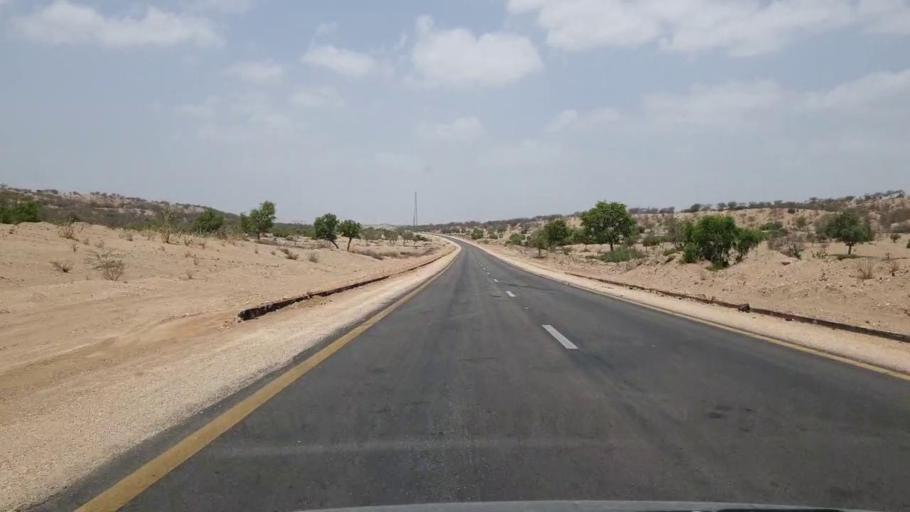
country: PK
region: Sindh
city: Mithi
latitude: 24.8350
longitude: 69.6303
